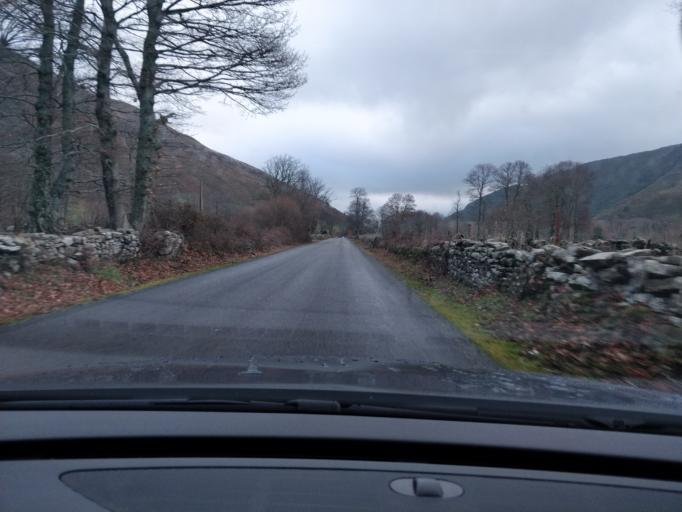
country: ES
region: Castille and Leon
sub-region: Provincia de Burgos
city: Espinosa de los Monteros
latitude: 43.1081
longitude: -3.5756
